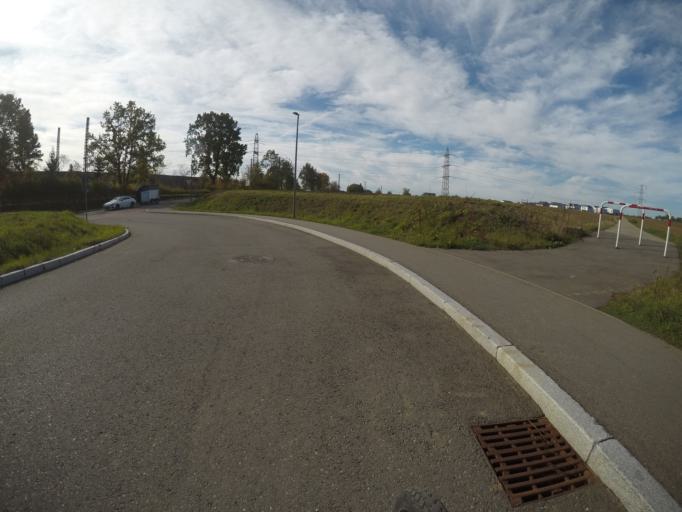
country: DE
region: Baden-Wuerttemberg
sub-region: Regierungsbezirk Stuttgart
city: Ehningen
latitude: 48.6668
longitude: 8.9515
